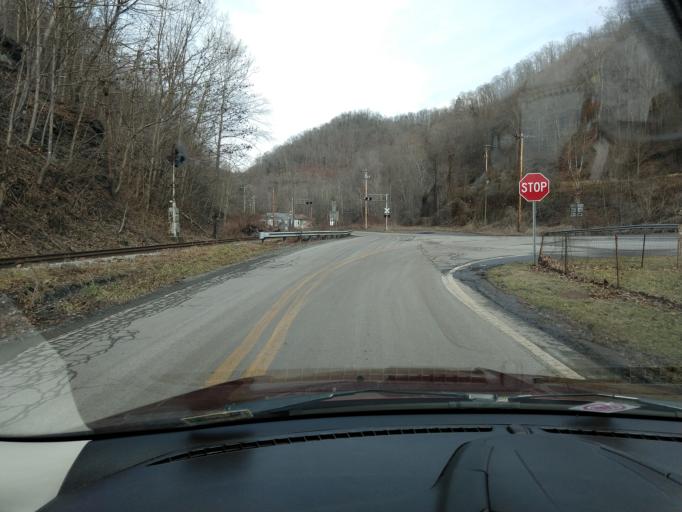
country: US
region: West Virginia
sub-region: McDowell County
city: Welch
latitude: 37.3222
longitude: -81.6906
